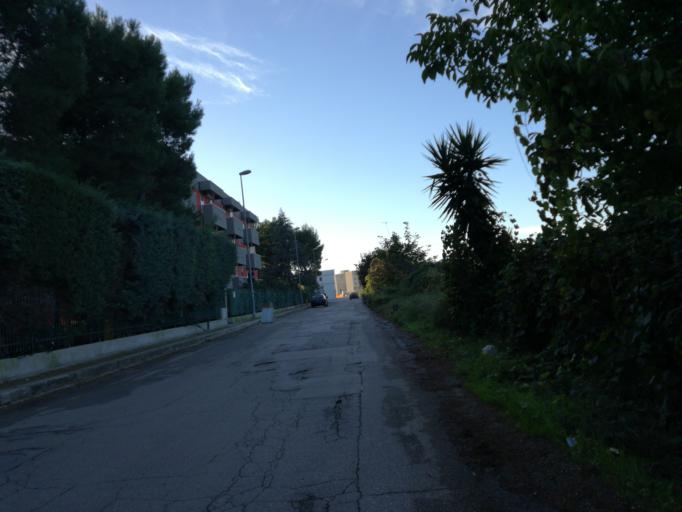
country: IT
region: Apulia
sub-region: Provincia di Bari
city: Adelfia
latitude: 41.0077
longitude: 16.8688
